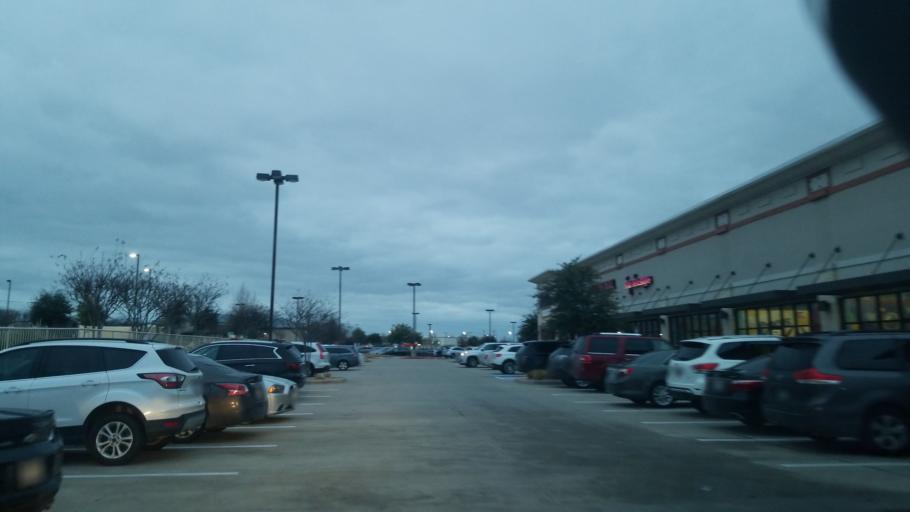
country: US
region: Texas
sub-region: Collin County
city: Frisco
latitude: 33.1208
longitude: -96.8024
